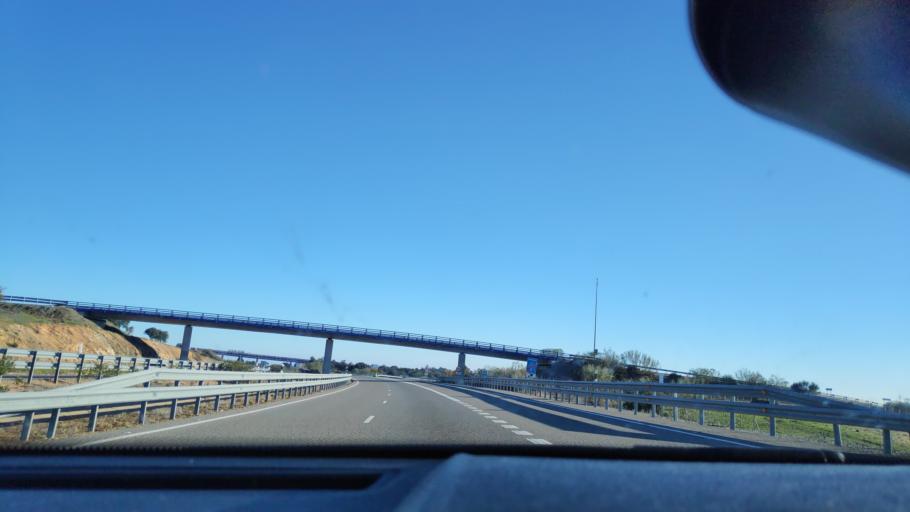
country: ES
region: Andalusia
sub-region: Provincia de Sevilla
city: Gerena
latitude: 37.6289
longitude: -6.1462
